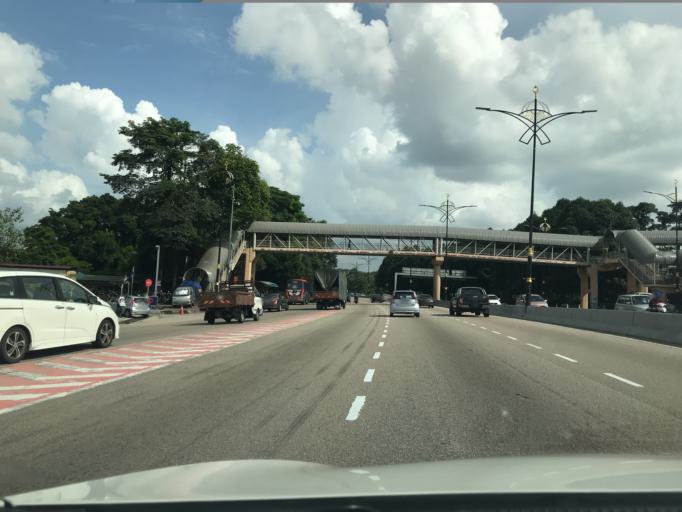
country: MY
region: Johor
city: Skudai
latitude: 1.5285
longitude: 103.6700
